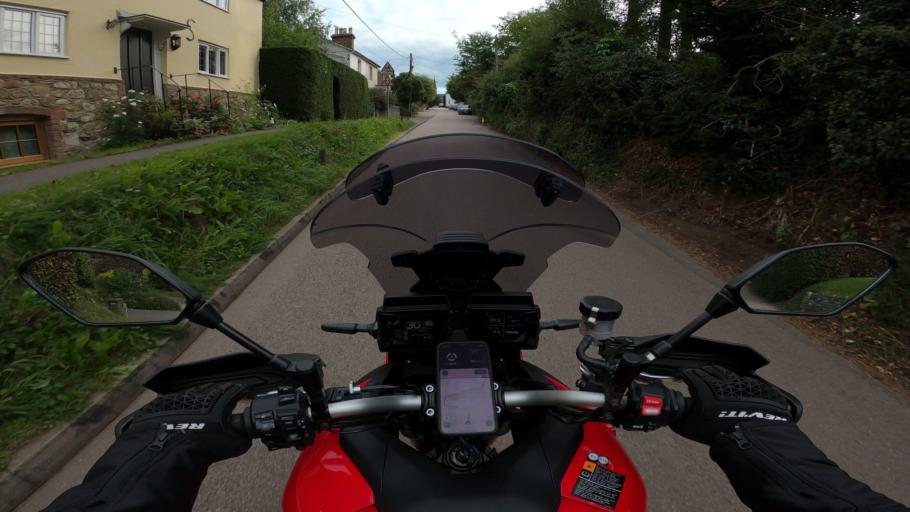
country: GB
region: England
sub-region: Kent
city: Westerham
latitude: 51.2476
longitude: 0.1267
